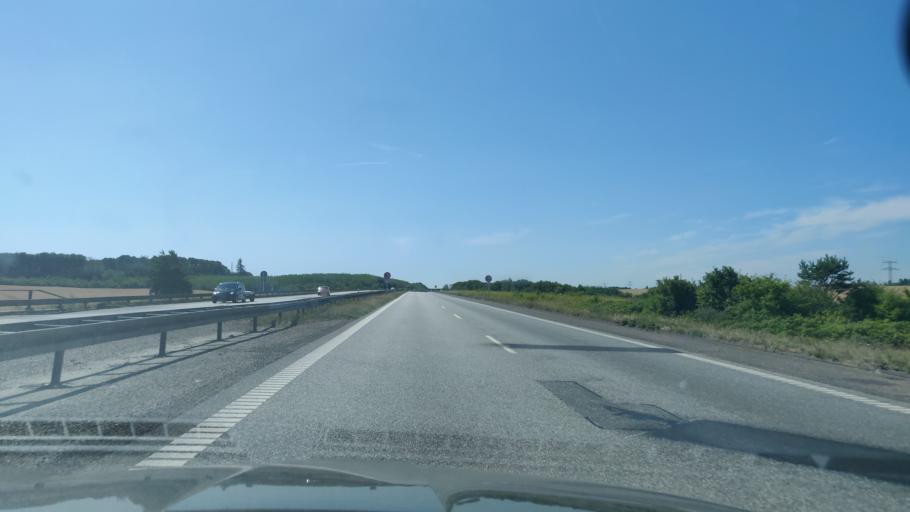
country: DK
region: North Denmark
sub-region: Alborg Kommune
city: Svenstrup
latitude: 56.9502
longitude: 9.8653
